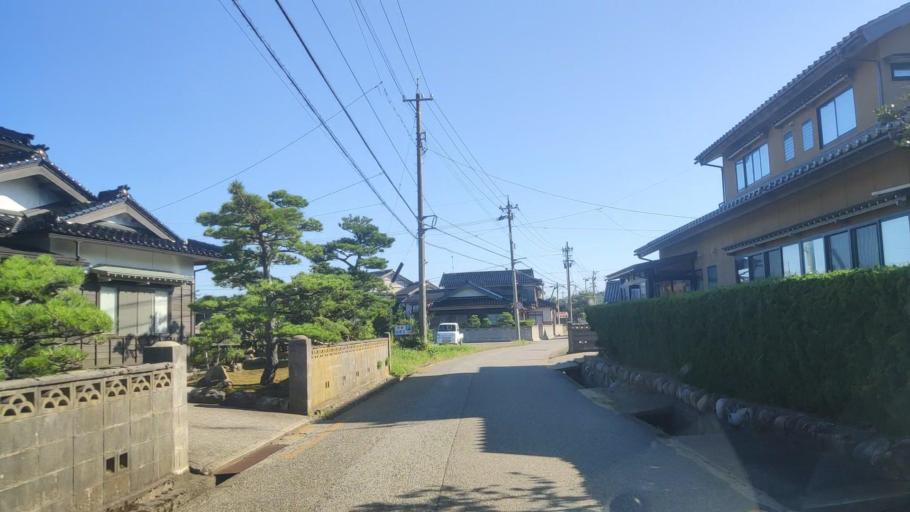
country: JP
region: Ishikawa
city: Hakui
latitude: 36.9517
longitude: 136.7650
